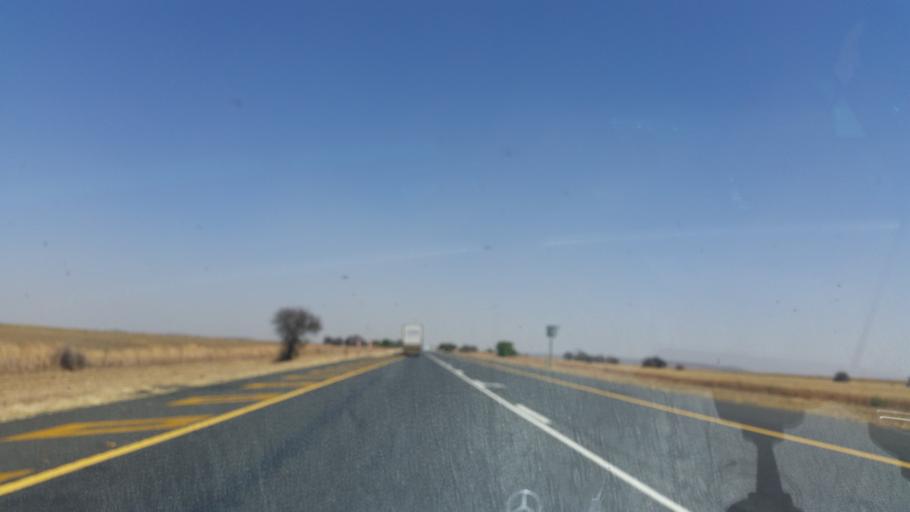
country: ZA
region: Orange Free State
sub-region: Lejweleputswa District Municipality
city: Winburg
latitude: -28.6482
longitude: 26.8791
